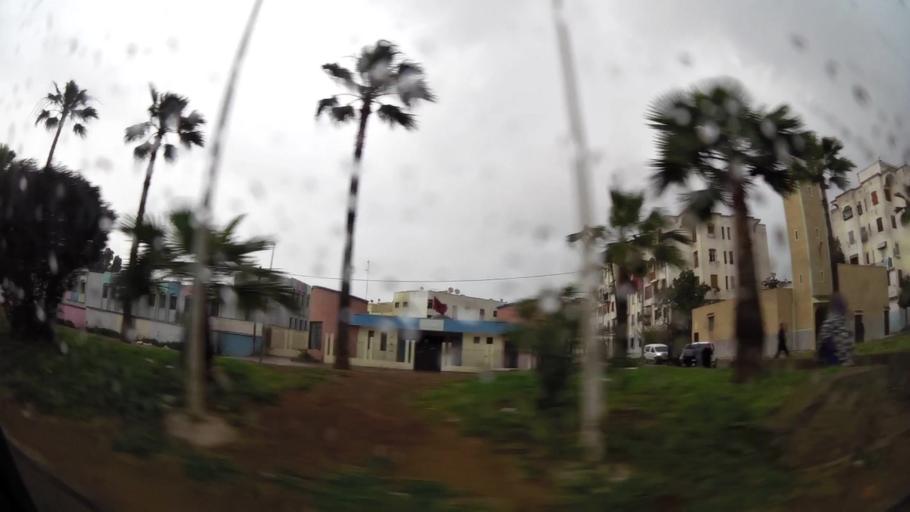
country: MA
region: Grand Casablanca
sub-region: Mediouna
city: Tit Mellil
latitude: 33.5718
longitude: -7.5276
